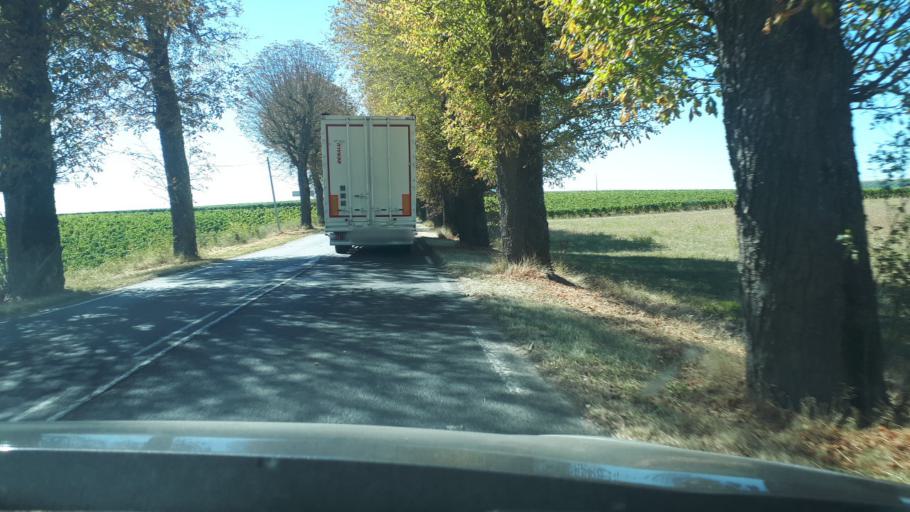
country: FR
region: Centre
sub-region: Departement du Cher
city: Sancerre
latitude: 47.3205
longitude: 2.8182
